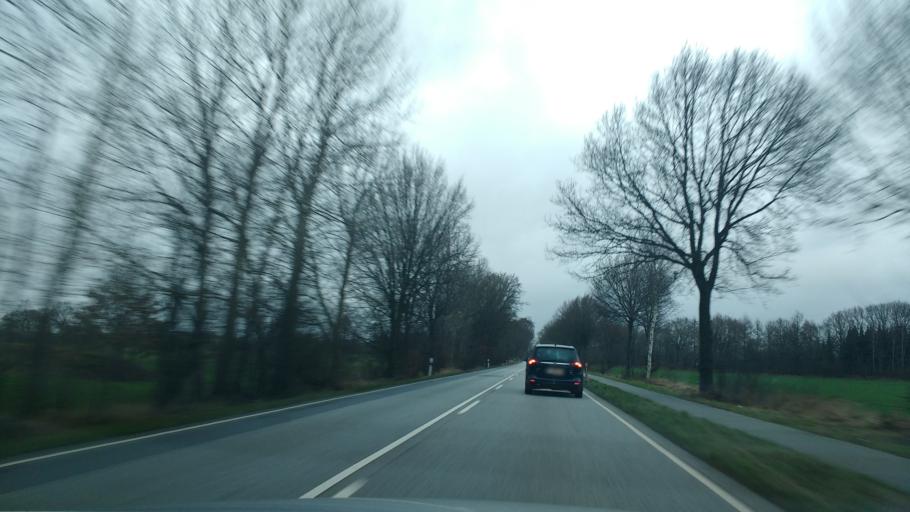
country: DE
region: Schleswig-Holstein
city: Schlotfeld
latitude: 53.9576
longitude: 9.5596
